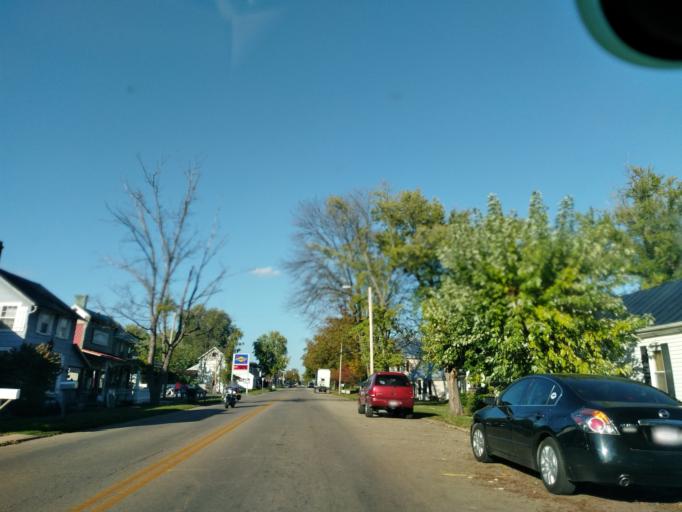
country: US
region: Ohio
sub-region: Ross County
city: Kingston
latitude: 39.4707
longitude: -82.9123
